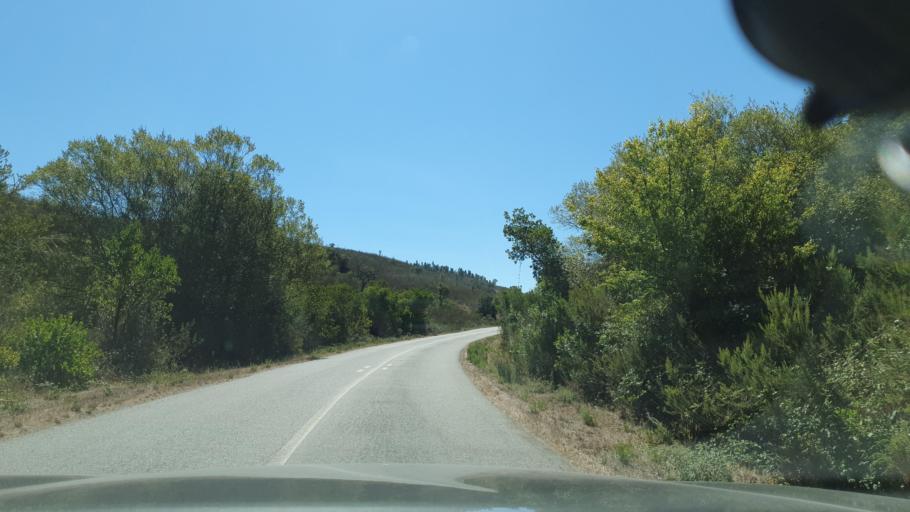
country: PT
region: Beja
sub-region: Odemira
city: Sao Teotonio
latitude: 37.4713
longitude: -8.6068
